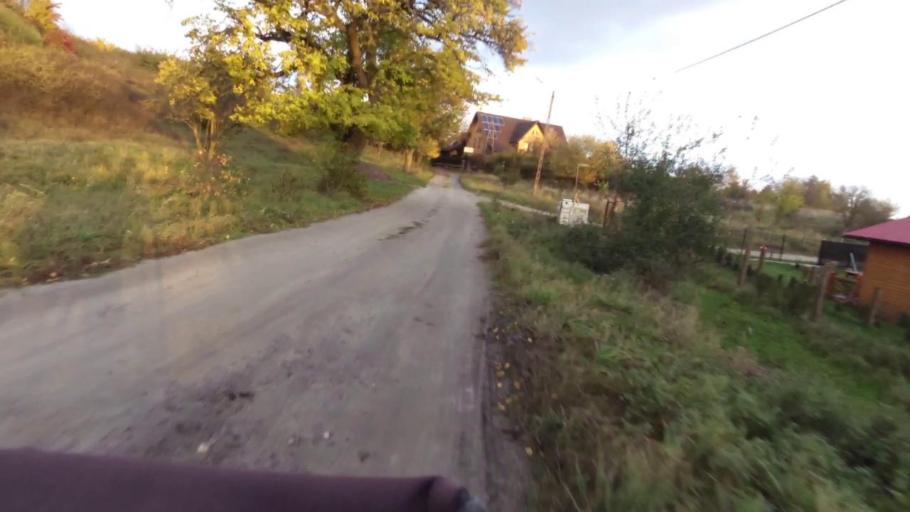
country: PL
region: West Pomeranian Voivodeship
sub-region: Powiat kamienski
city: Miedzyzdroje
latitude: 53.8655
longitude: 14.4362
